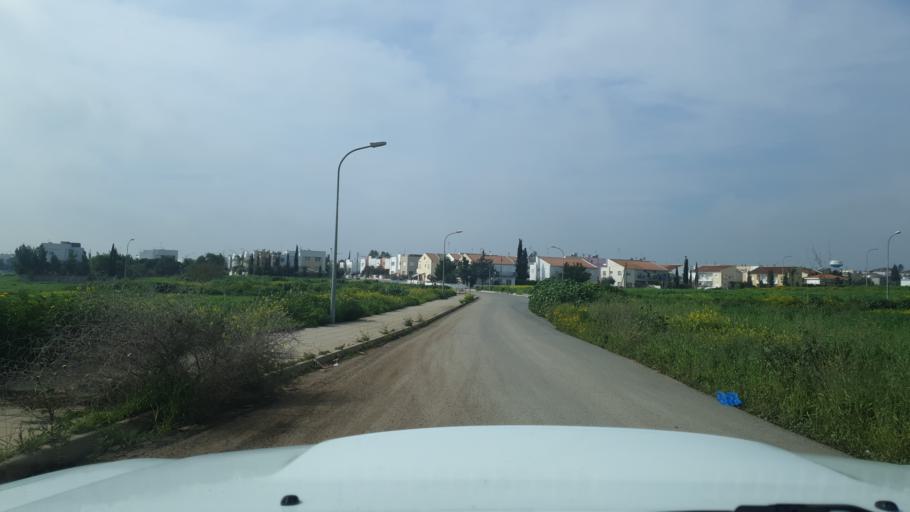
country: CY
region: Lefkosia
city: Nicosia
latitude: 35.1236
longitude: 33.3521
